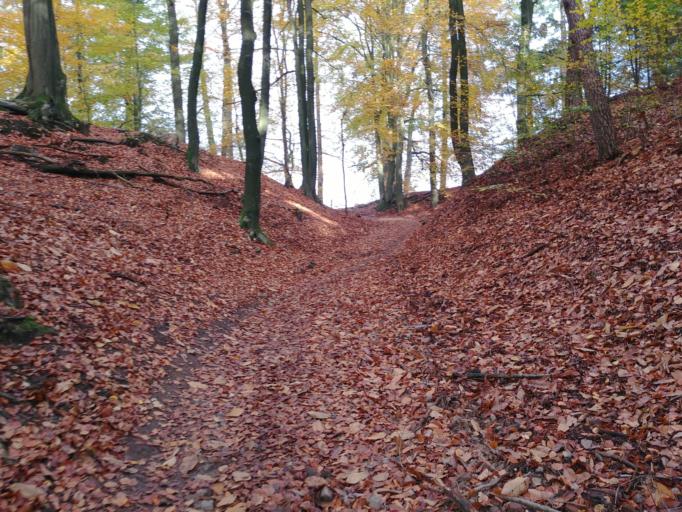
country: NL
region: Gelderland
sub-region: Gemeente Rheden
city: De Steeg
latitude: 52.0281
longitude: 6.0503
